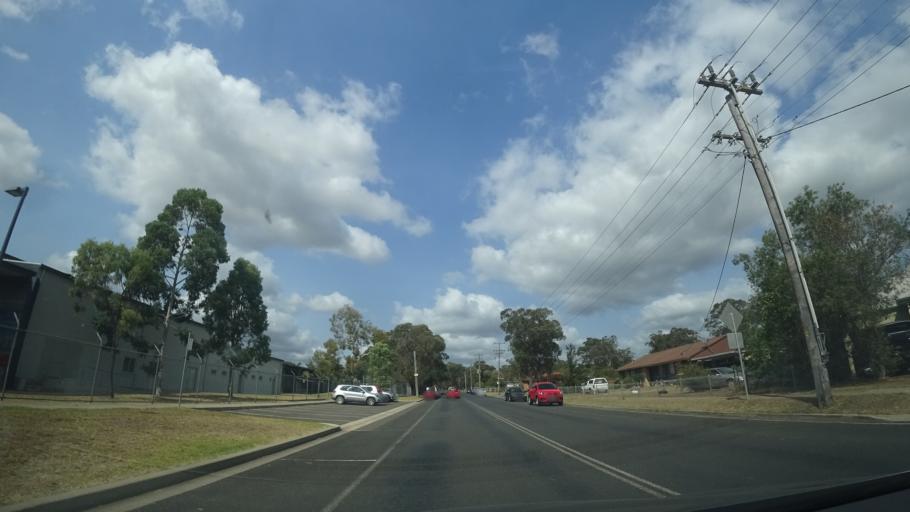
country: AU
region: New South Wales
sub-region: Wollondilly
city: Picton
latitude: -34.2070
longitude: 150.5685
